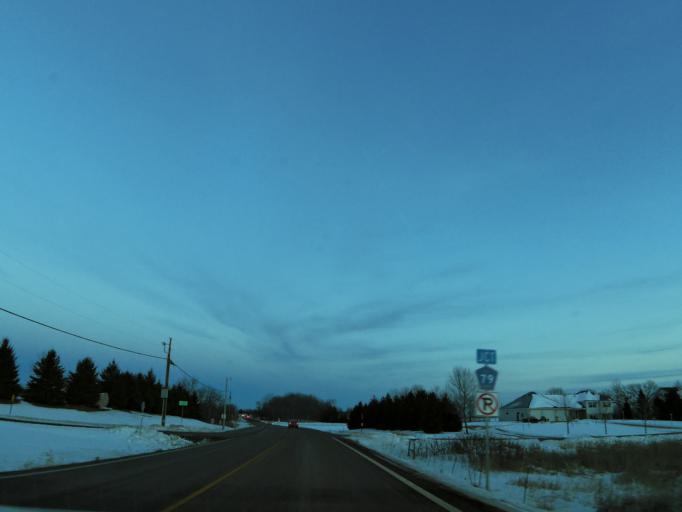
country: US
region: Minnesota
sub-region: Scott County
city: Shakopee
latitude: 44.7328
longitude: -93.5315
